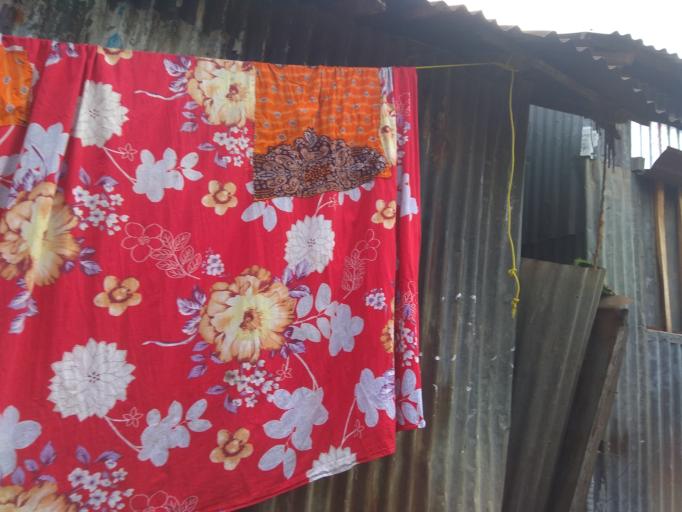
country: BD
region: Dhaka
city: Tungi
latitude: 23.8129
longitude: 90.3907
